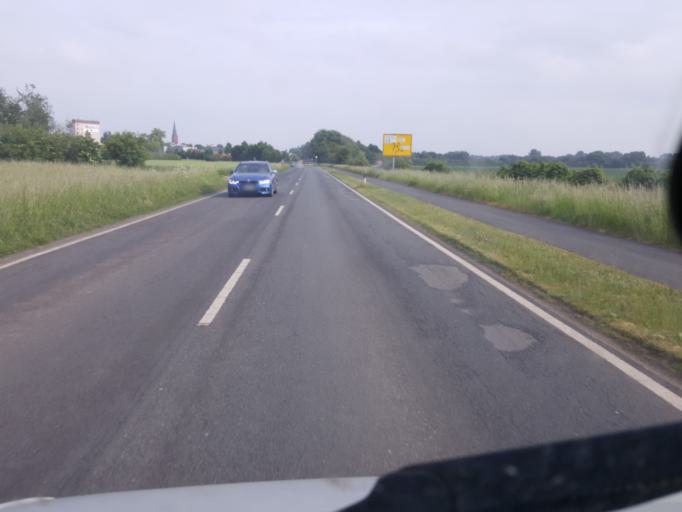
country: DE
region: Lower Saxony
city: Nienburg
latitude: 52.6479
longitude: 9.1934
